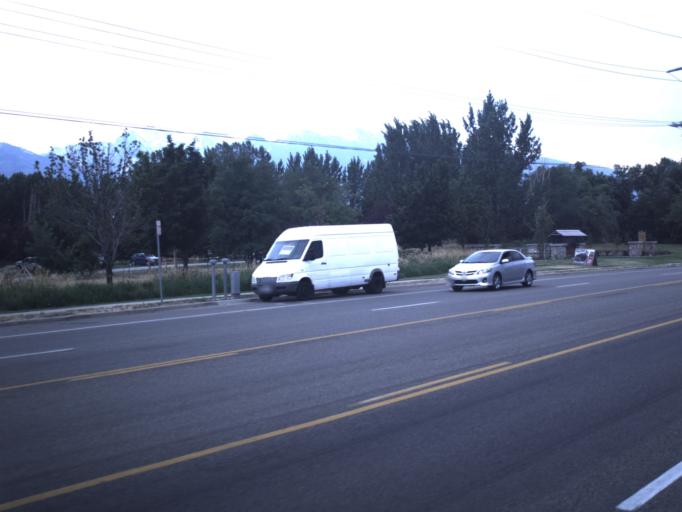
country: US
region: Utah
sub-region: Salt Lake County
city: Murray
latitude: 40.6344
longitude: -111.8661
